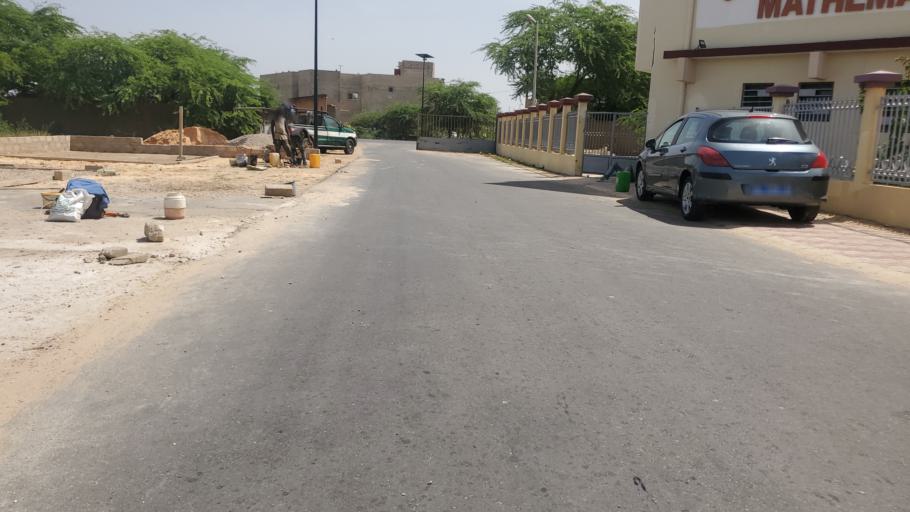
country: SN
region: Saint-Louis
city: Saint-Louis
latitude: 16.0563
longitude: -16.4265
